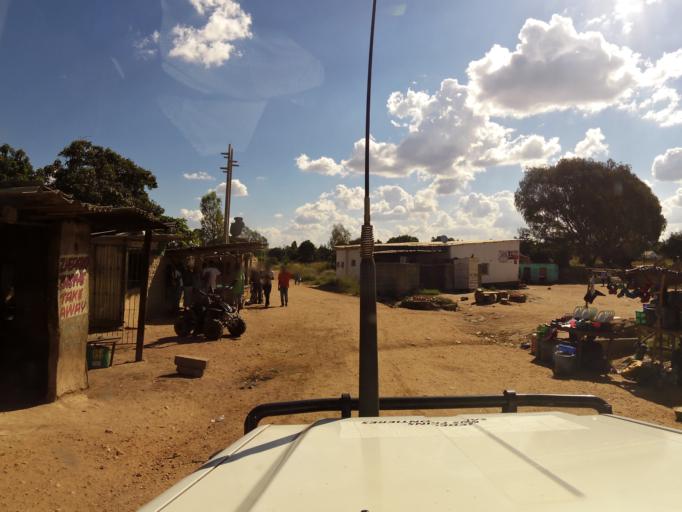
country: ZW
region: Harare
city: Epworth
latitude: -17.8755
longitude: 31.1359
